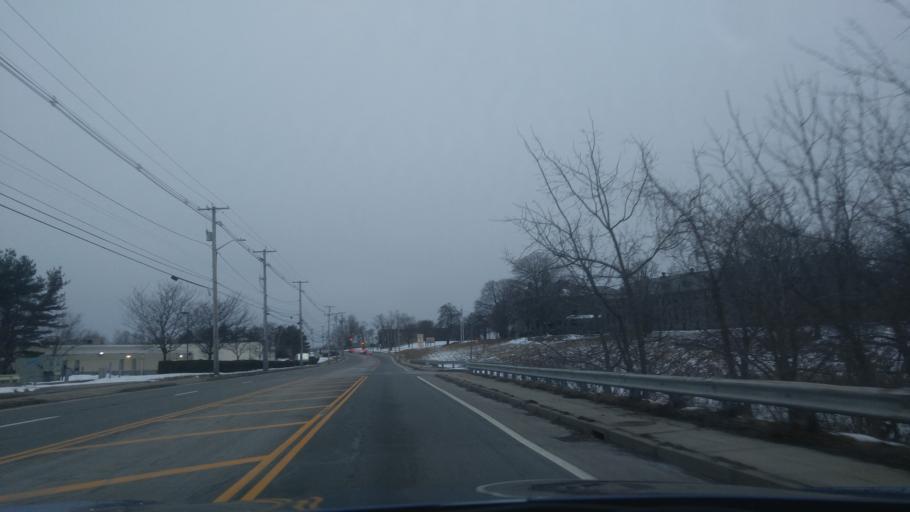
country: US
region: Rhode Island
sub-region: Providence County
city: Cranston
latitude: 41.7429
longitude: -71.4579
